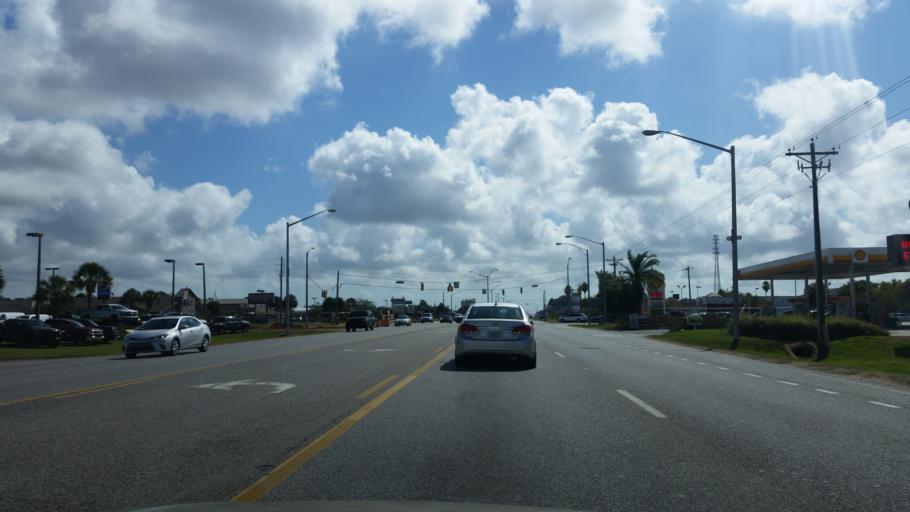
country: US
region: Alabama
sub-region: Baldwin County
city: Foley
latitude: 30.3823
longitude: -87.6834
